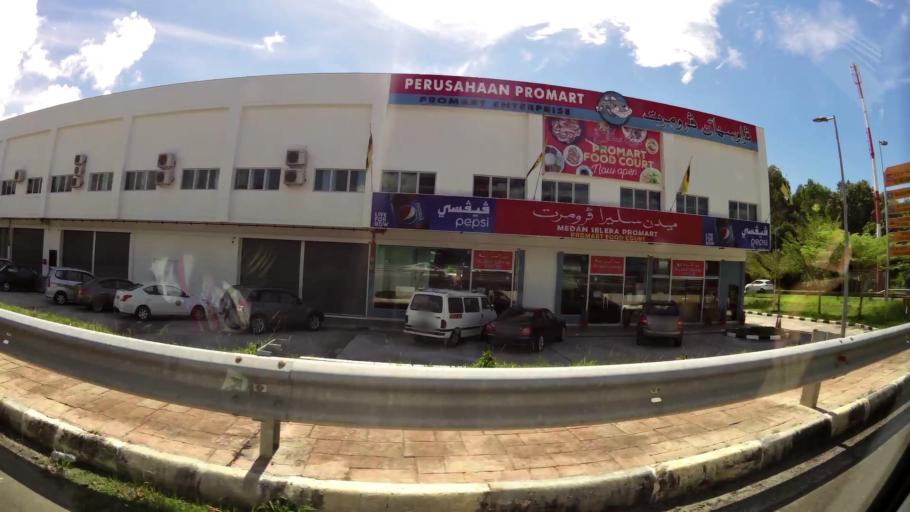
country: BN
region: Brunei and Muara
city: Bandar Seri Begawan
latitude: 4.9757
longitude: 114.9550
